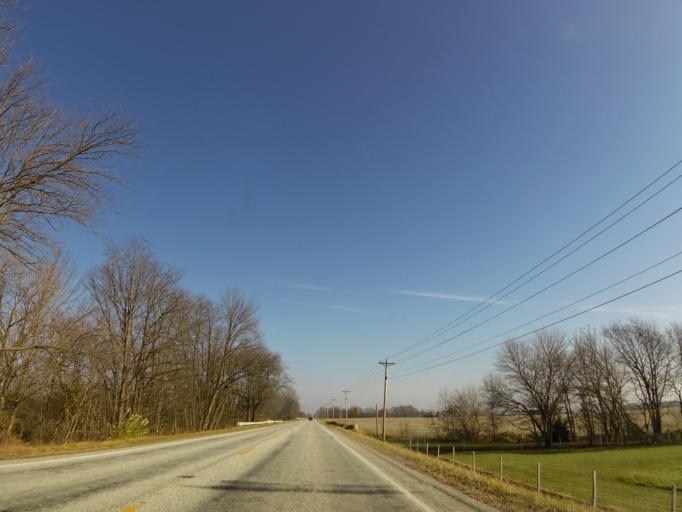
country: US
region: Indiana
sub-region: Shelby County
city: Shelbyville
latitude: 39.5362
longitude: -85.7130
